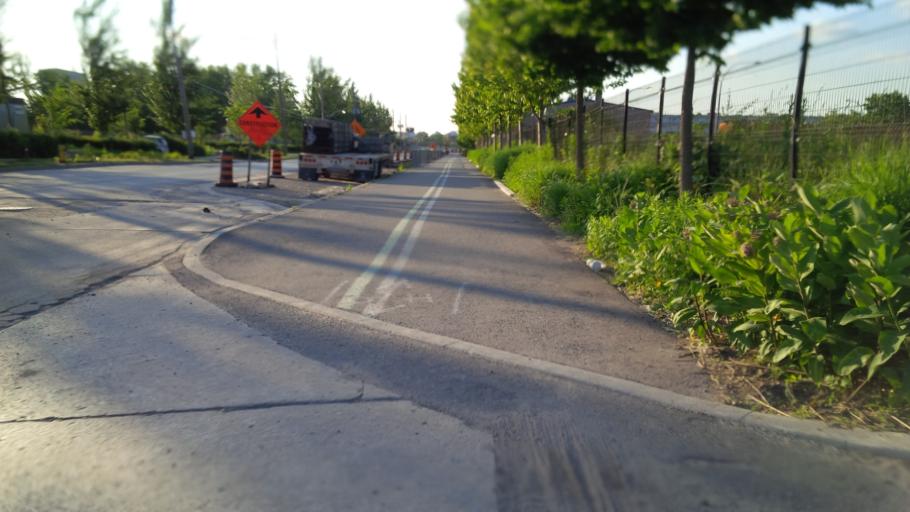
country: CA
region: Ontario
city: Toronto
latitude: 43.6541
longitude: -79.3242
